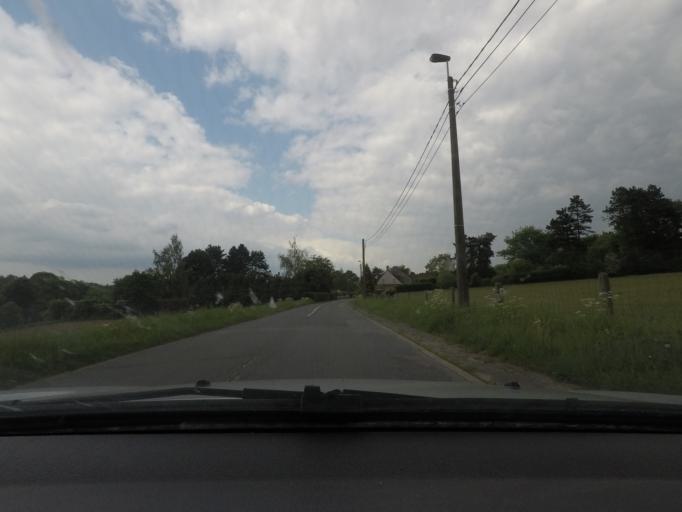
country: BE
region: Wallonia
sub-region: Province du Hainaut
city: Basse Lasne
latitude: 50.6663
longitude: 4.4944
